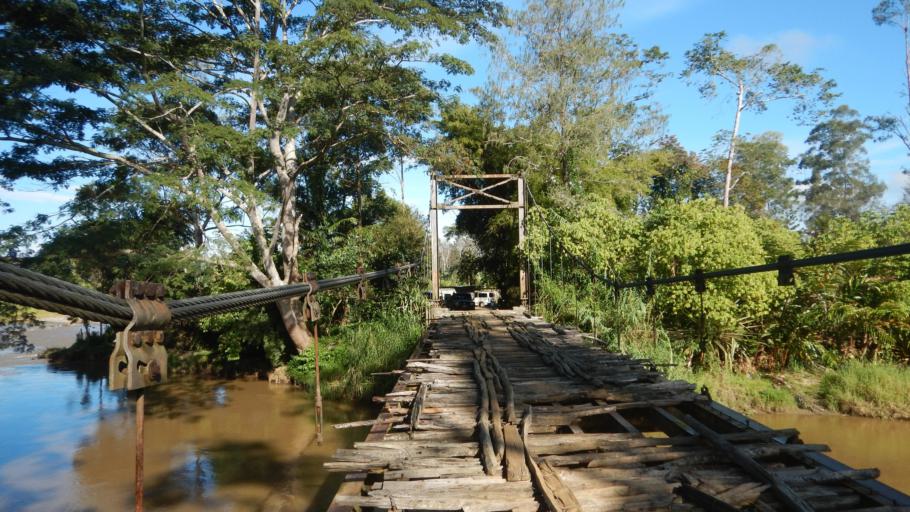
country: PG
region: Western Highlands
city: Rauna
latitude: -5.7971
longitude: 144.3590
